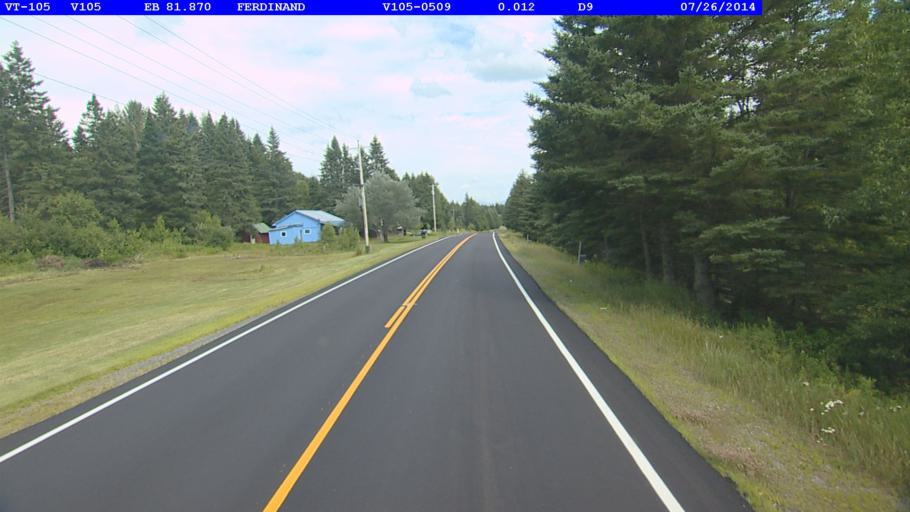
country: US
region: New Hampshire
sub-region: Coos County
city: Stratford
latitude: 44.7857
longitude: -71.8030
